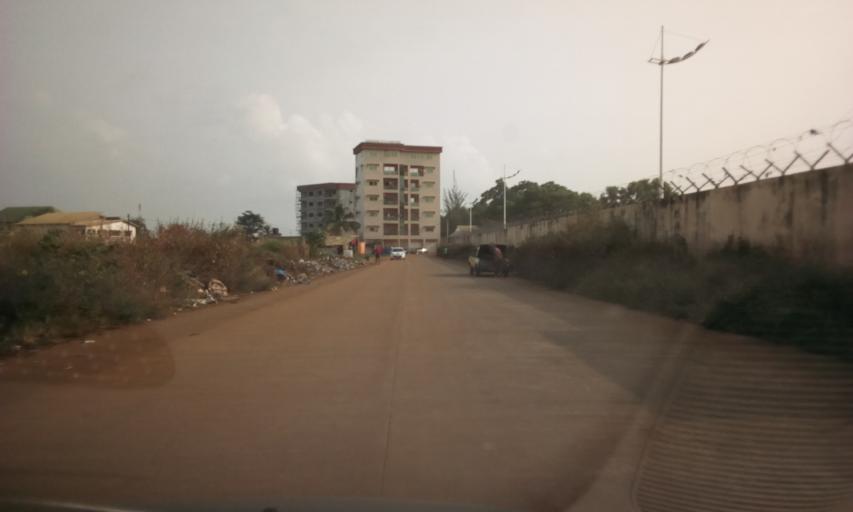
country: GN
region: Conakry
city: Conakry
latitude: 9.6267
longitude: -13.6277
